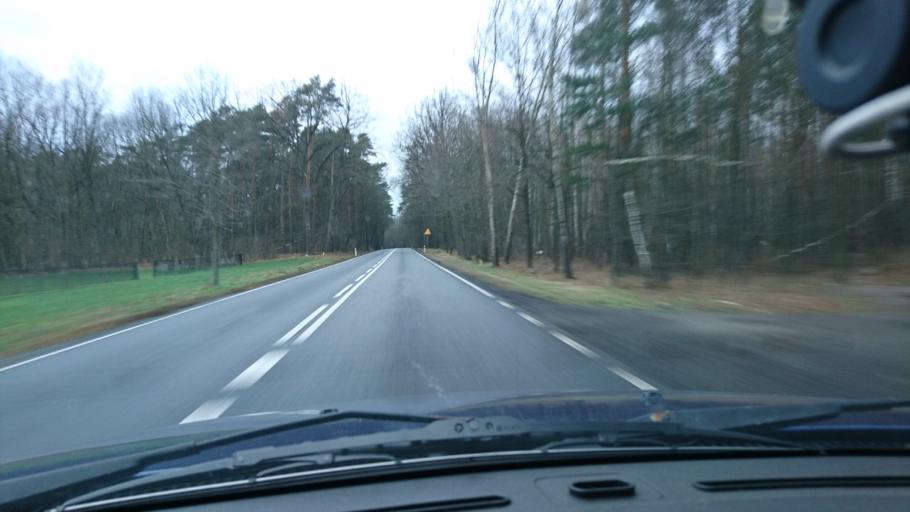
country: PL
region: Opole Voivodeship
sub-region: Powiat kluczborski
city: Kluczbork
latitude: 50.9423
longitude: 18.3240
